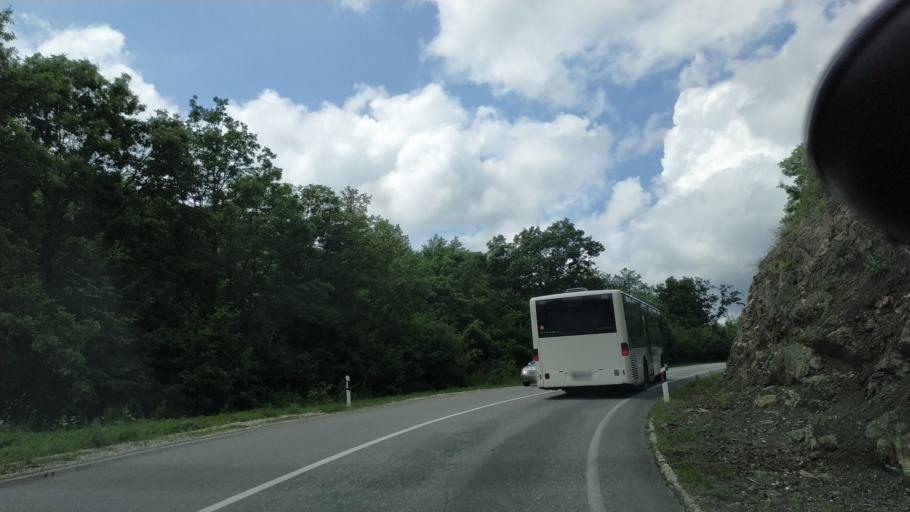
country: RS
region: Central Serbia
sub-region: Borski Okrug
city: Bor
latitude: 44.0557
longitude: 22.0660
